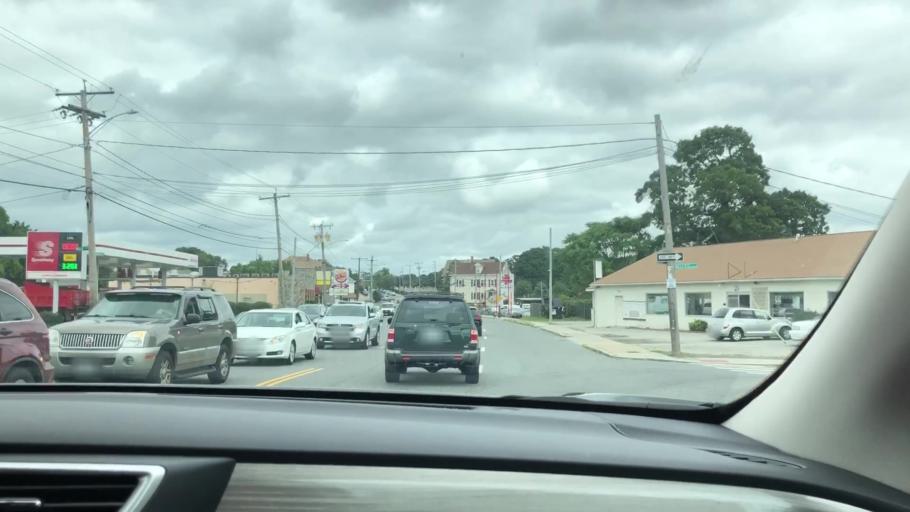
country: US
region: Rhode Island
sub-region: Providence County
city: Providence
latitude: 41.8572
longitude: -71.4108
